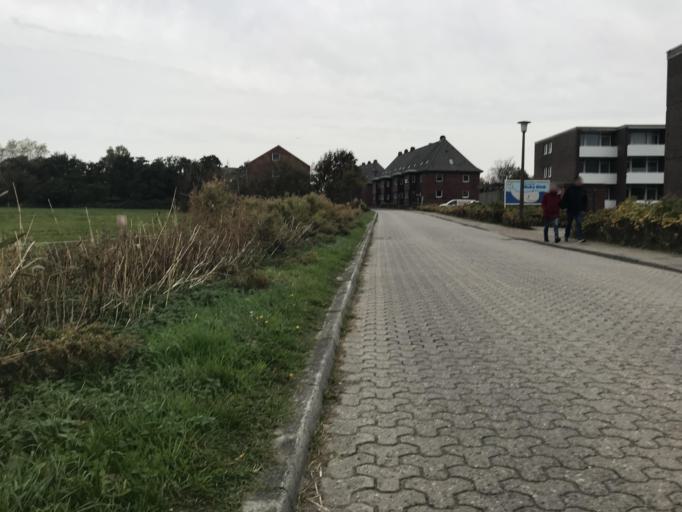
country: DE
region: Lower Saxony
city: Borkum
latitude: 53.5905
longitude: 6.6734
